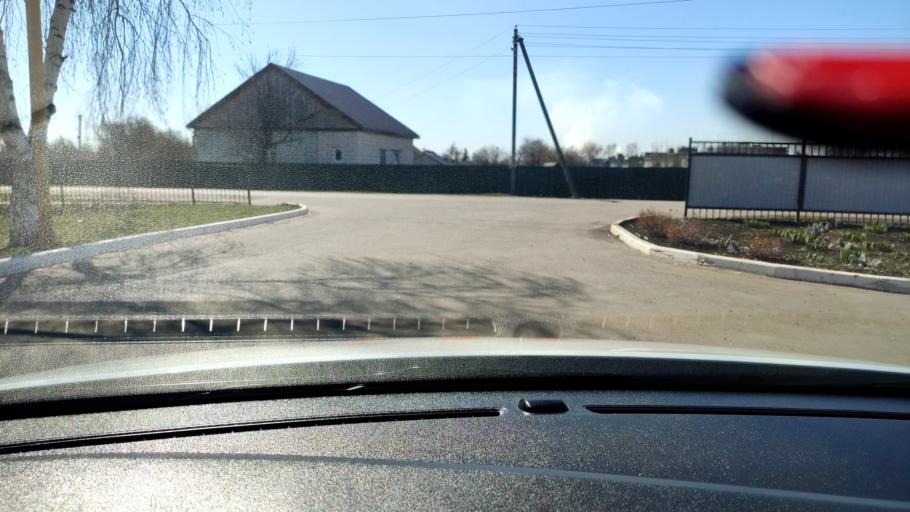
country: RU
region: Voronezj
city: Ramon'
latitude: 51.9834
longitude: 39.2240
